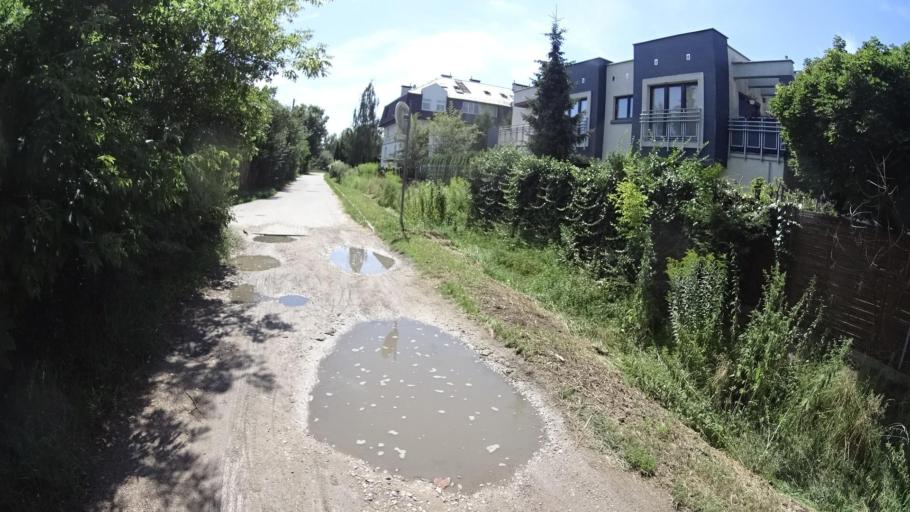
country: PL
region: Masovian Voivodeship
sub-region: Powiat piaseczynski
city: Mysiadlo
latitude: 52.1349
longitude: 21.0124
